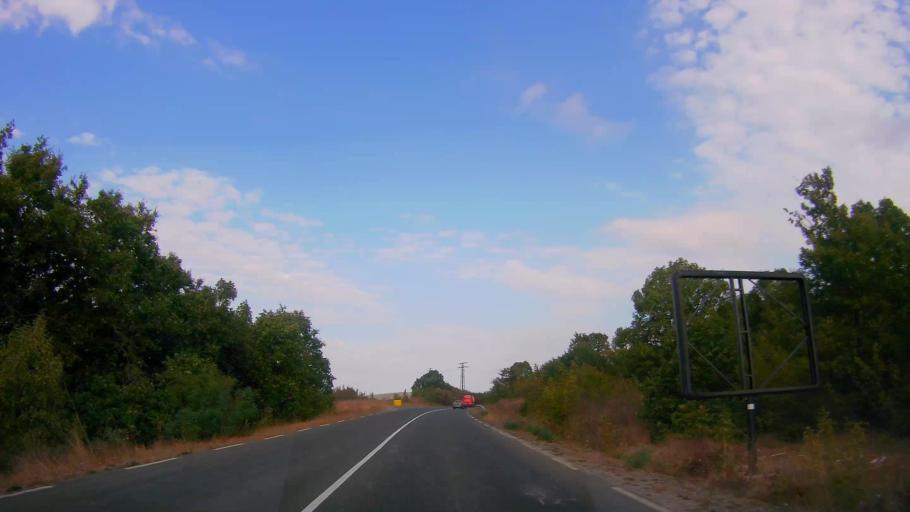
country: BG
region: Burgas
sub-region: Obshtina Sozopol
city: Sozopol
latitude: 42.3684
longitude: 27.6861
